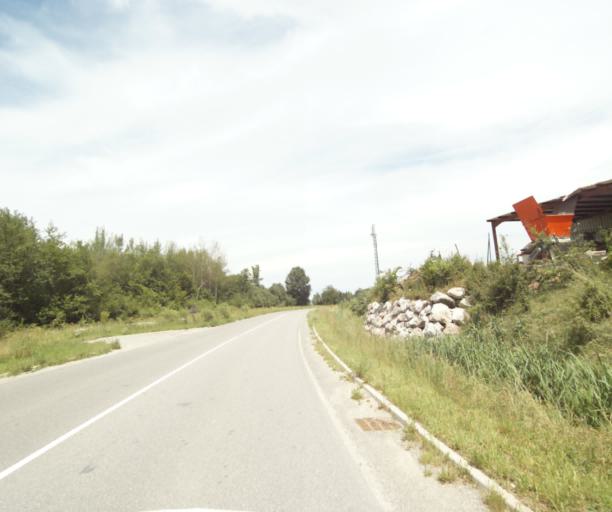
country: FR
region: Rhone-Alpes
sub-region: Departement de la Haute-Savoie
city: Margencel
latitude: 46.3248
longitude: 6.4354
